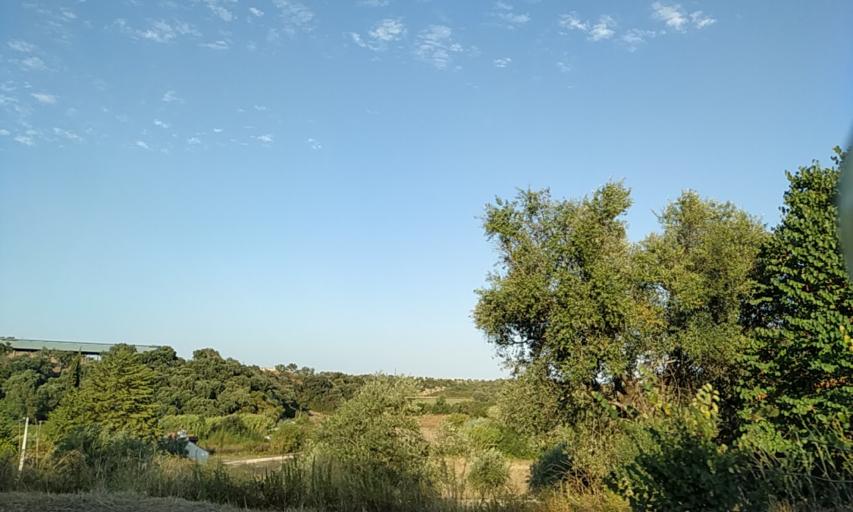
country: PT
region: Santarem
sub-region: Alcanena
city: Alcanena
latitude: 39.3581
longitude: -8.6510
